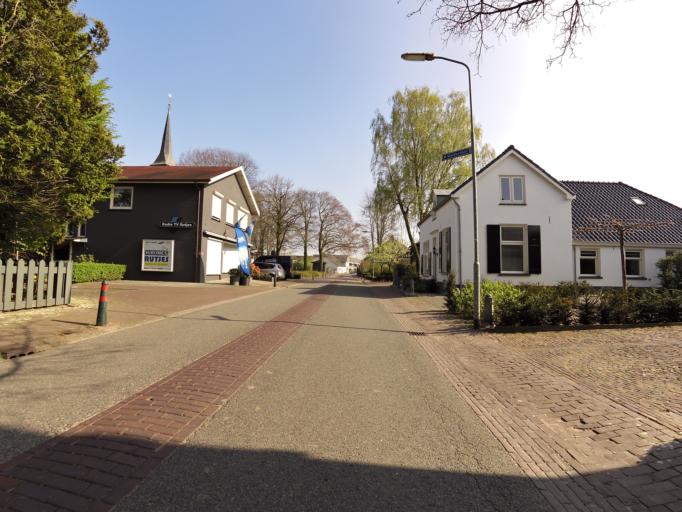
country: NL
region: Gelderland
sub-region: Gemeente Brummen
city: Brummen
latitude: 52.0650
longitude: 6.1859
